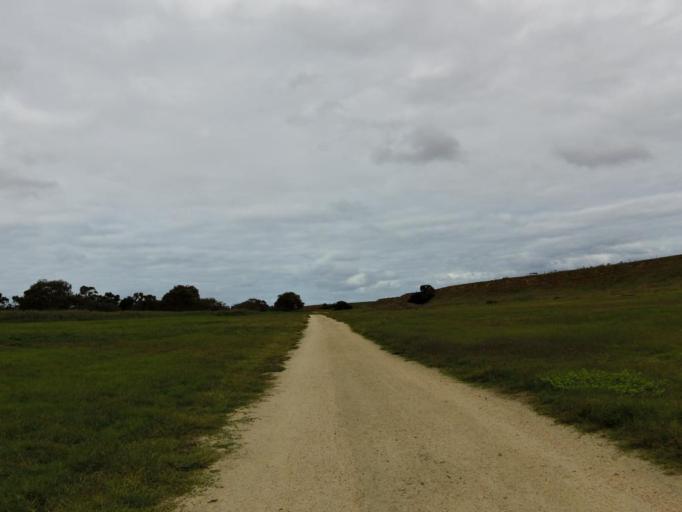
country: AU
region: Victoria
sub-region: Wyndham
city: Werribee
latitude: -37.9366
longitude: 144.6622
